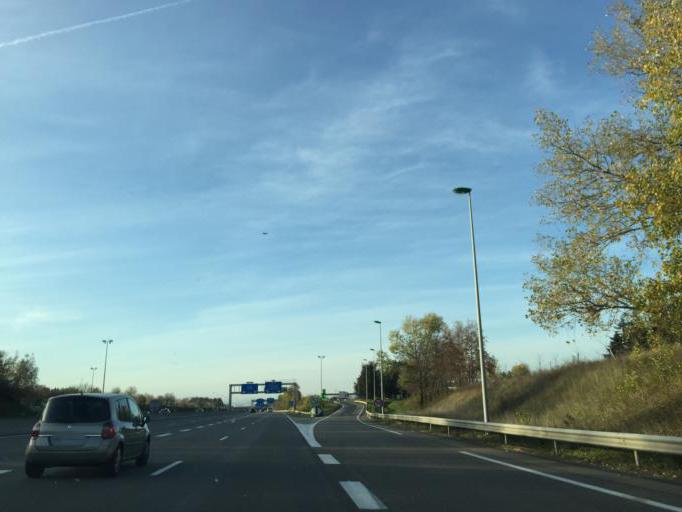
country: FR
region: Rhone-Alpes
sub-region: Departement du Rhone
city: Saint-Bonnet-de-Mure
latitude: 45.6957
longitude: 4.9809
